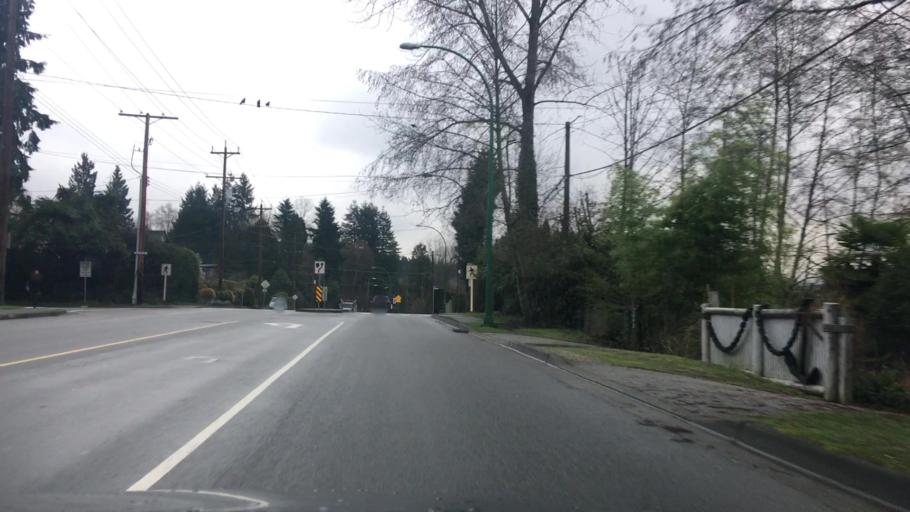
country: CA
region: British Columbia
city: Burnaby
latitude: 49.3089
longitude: -122.9947
